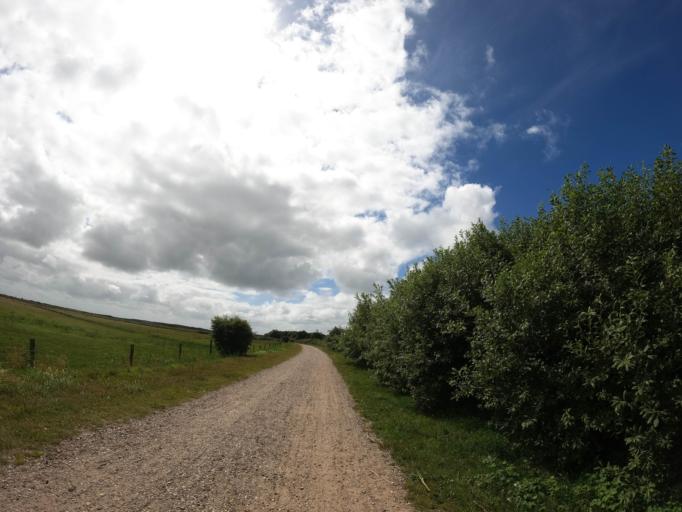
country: DE
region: Schleswig-Holstein
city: Tinnum
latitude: 54.8955
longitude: 8.3187
